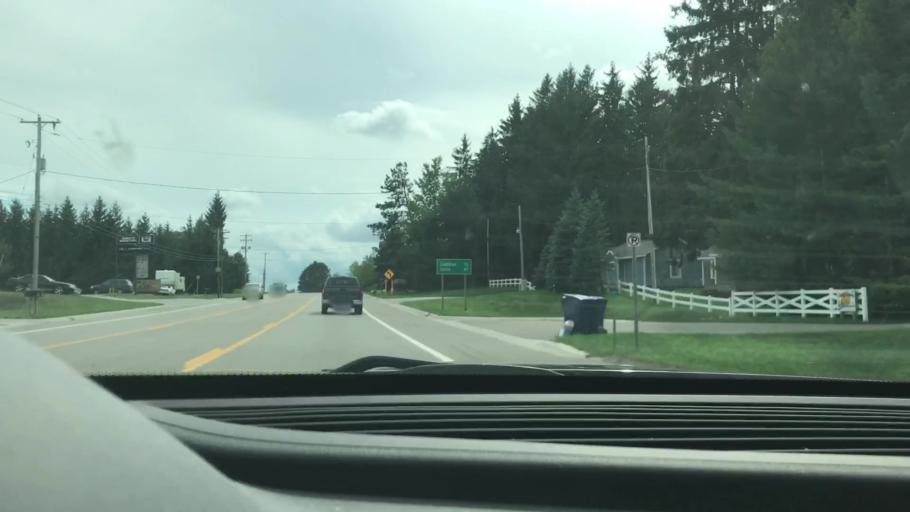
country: US
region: Michigan
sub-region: Missaukee County
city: Lake City
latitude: 44.3168
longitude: -85.2135
